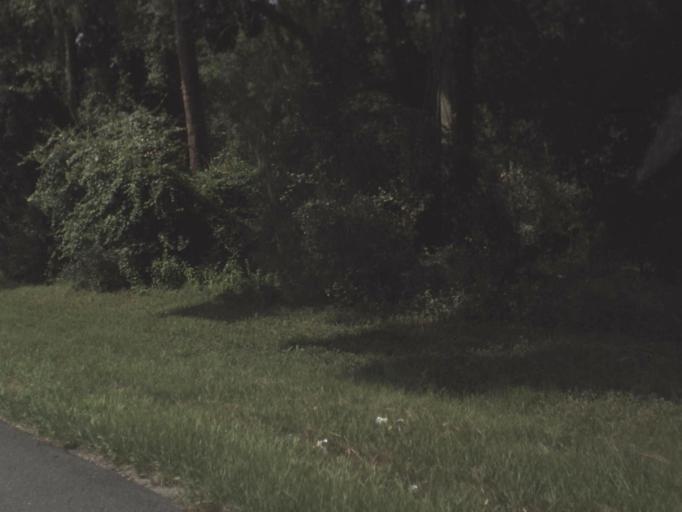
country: US
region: Florida
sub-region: Citrus County
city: Inverness Highlands North
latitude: 28.8660
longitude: -82.3578
